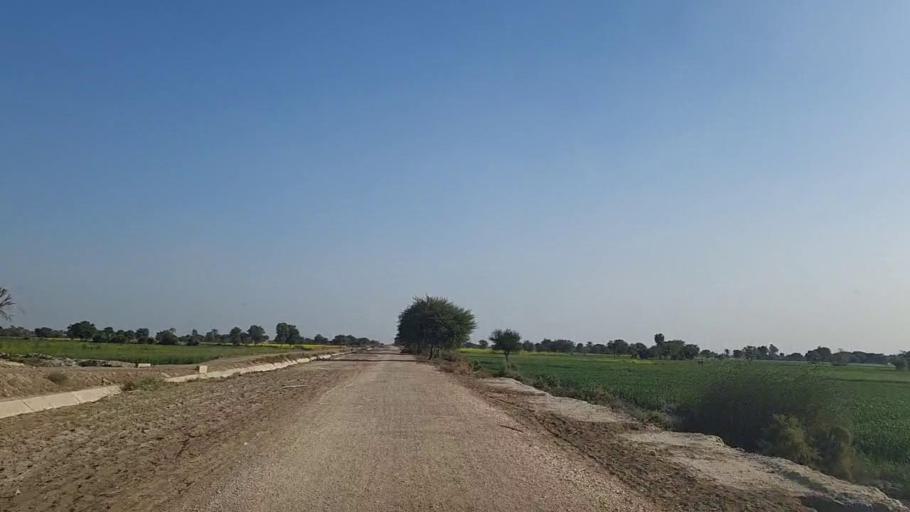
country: PK
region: Sindh
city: Shahpur Chakar
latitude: 26.2042
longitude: 68.6448
